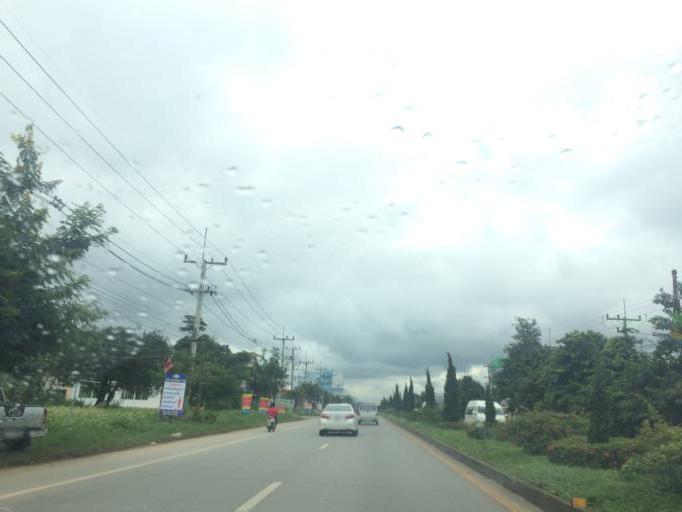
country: TH
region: Chiang Rai
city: Chiang Rai
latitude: 20.0091
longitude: 99.8682
